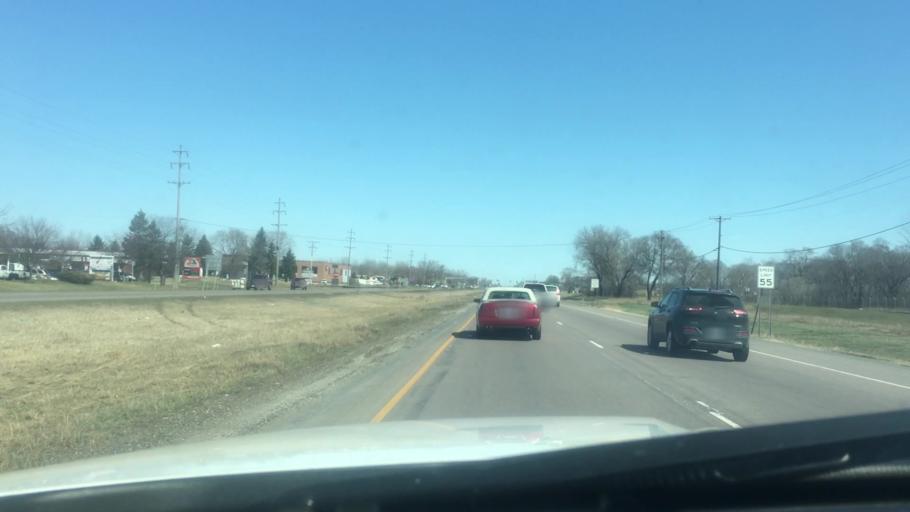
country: US
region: Minnesota
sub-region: Anoka County
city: Blaine
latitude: 45.1450
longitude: -93.2352
